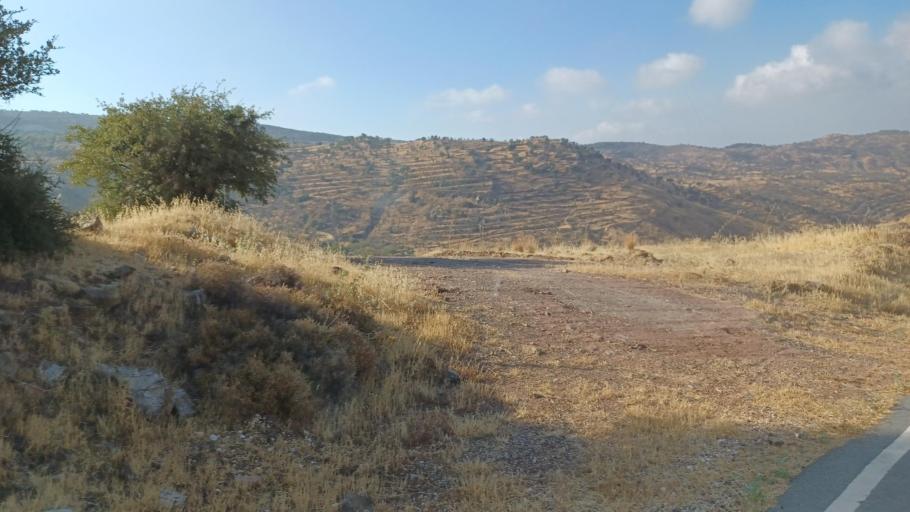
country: CY
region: Pafos
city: Mesogi
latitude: 34.8674
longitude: 32.6061
